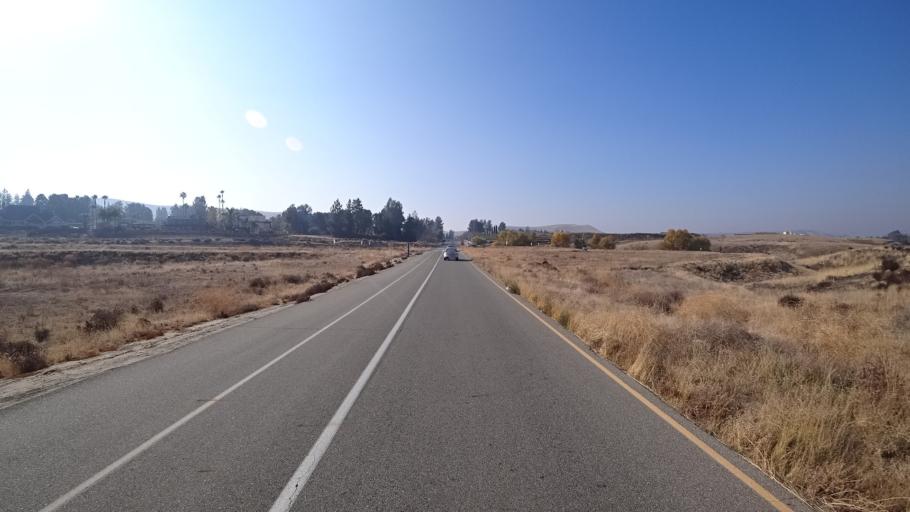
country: US
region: California
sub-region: Kern County
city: Oildale
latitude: 35.4343
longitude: -118.8641
